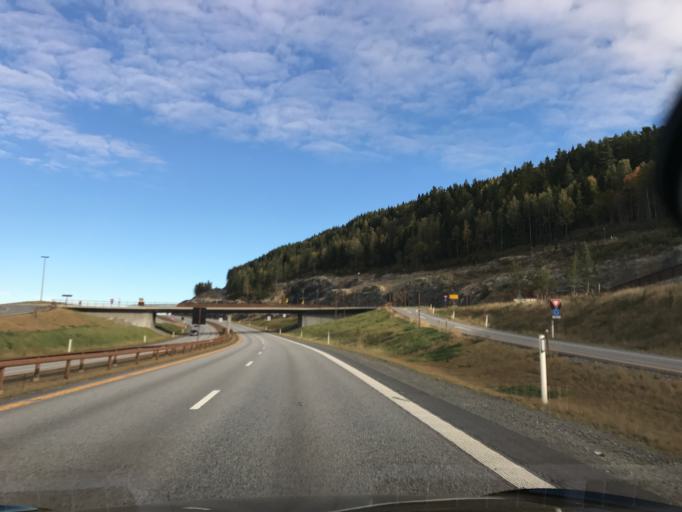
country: NO
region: Akershus
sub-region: Eidsvoll
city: Eidsvoll
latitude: 60.5131
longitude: 11.2440
